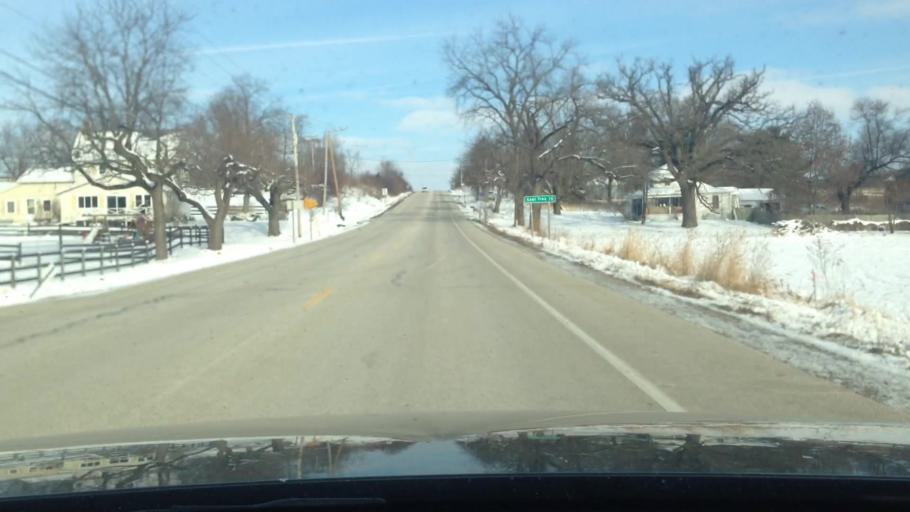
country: US
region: Wisconsin
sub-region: Walworth County
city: Lake Geneva
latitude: 42.6459
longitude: -88.4136
